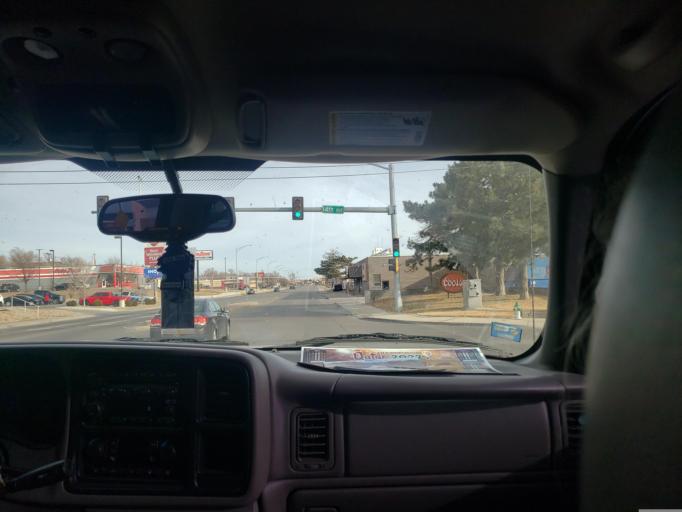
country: US
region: Kansas
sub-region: Ford County
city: Dodge City
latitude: 37.7536
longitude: -100.0331
